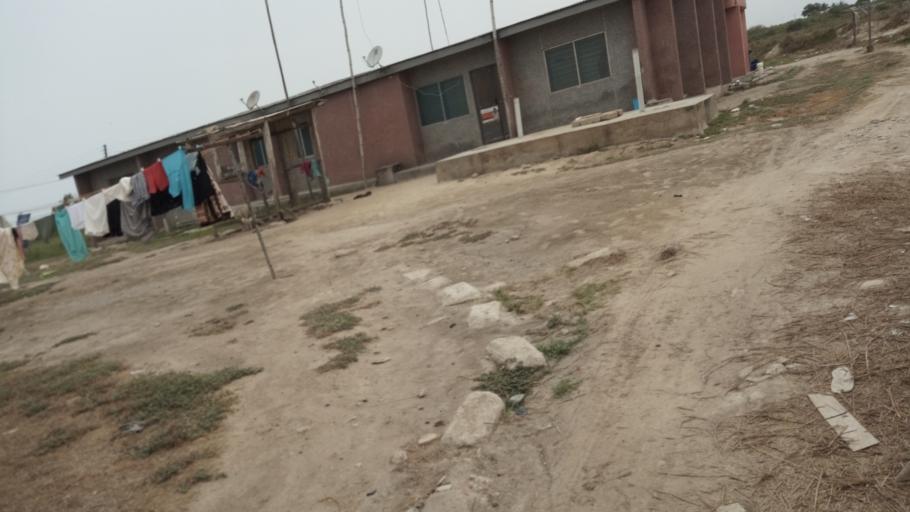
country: GH
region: Central
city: Winneba
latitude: 5.3478
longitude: -0.6347
